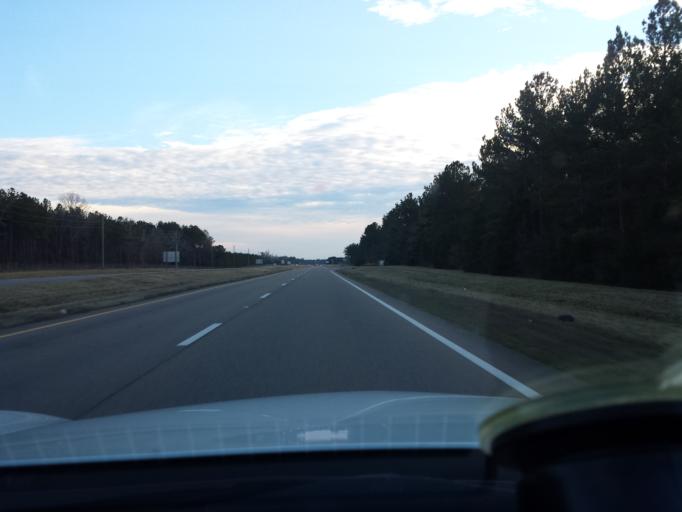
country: US
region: Mississippi
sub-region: Oktibbeha County
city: Starkville
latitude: 33.4310
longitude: -88.8540
